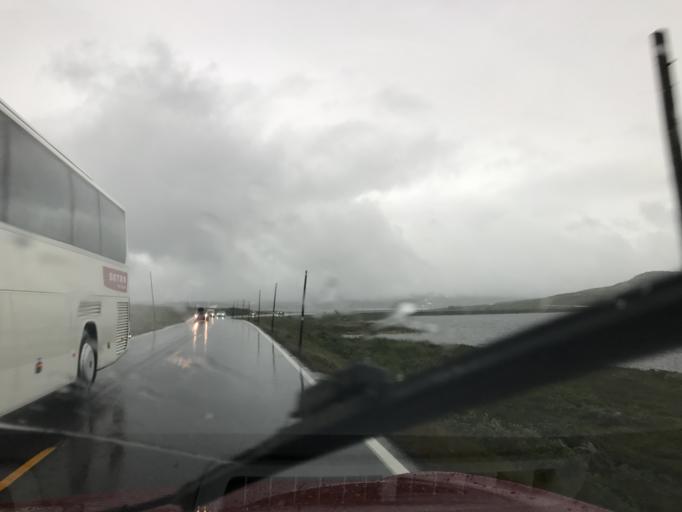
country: NO
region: Buskerud
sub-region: Hol
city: Geilo
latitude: 60.4530
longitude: 7.8190
